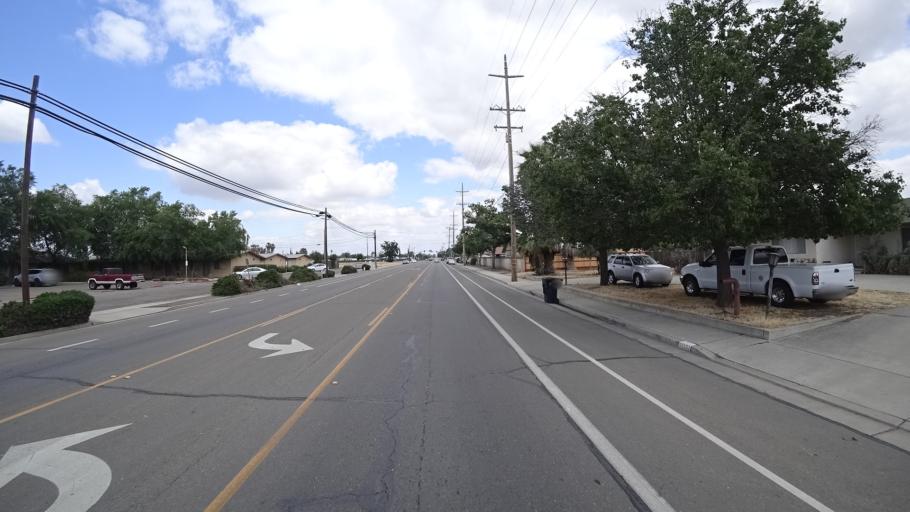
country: US
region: California
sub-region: Kings County
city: Hanford
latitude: 36.3134
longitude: -119.6581
